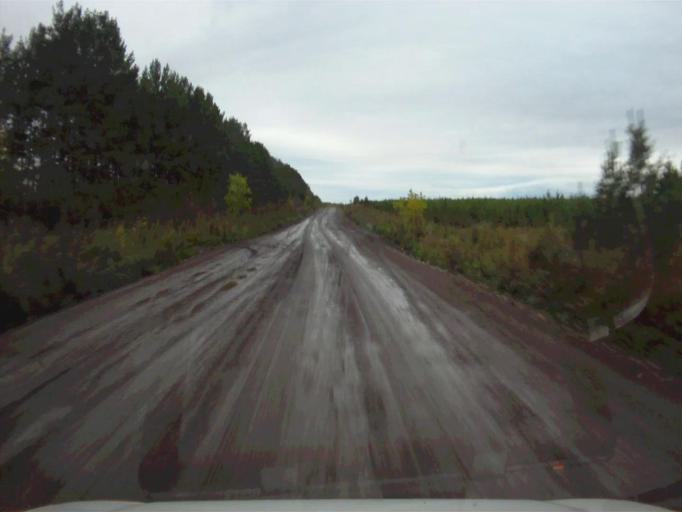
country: RU
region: Chelyabinsk
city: Nyazepetrovsk
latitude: 56.1437
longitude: 59.2864
